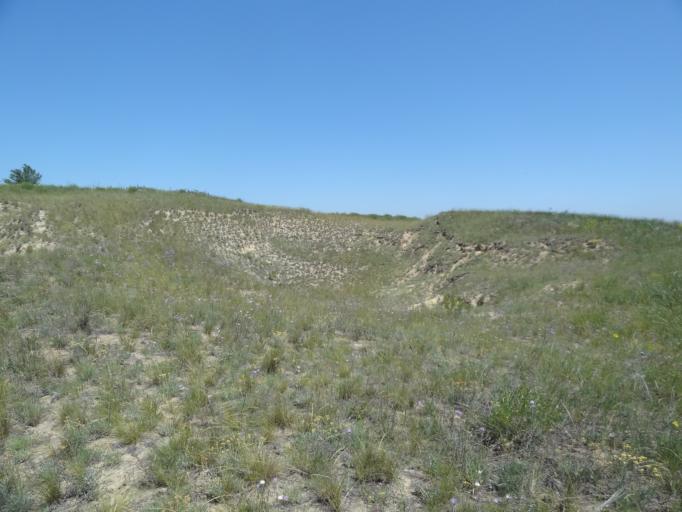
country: RU
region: Saratov
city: Krasnyy Oktyabr'
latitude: 51.2971
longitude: 45.5390
